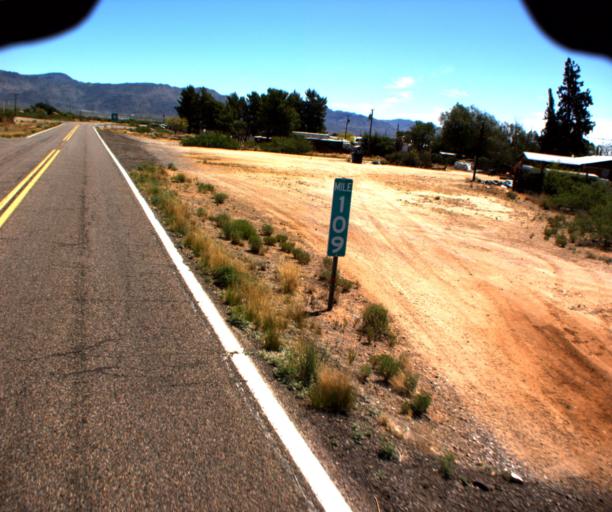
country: US
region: Arizona
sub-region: Yavapai County
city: Congress
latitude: 34.1612
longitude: -112.8551
